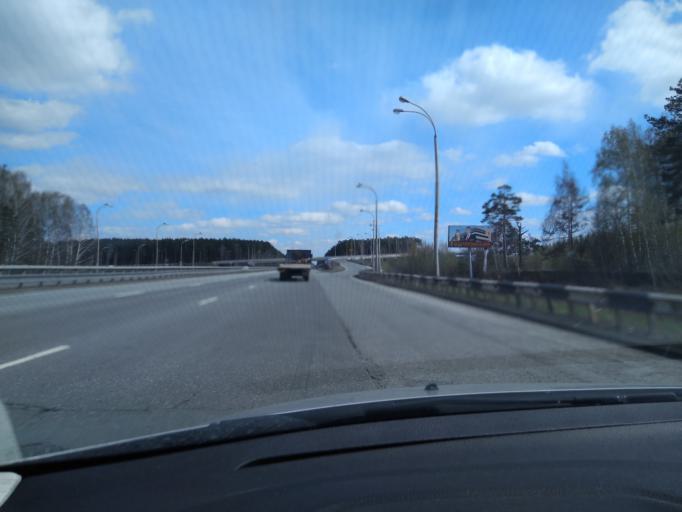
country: RU
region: Sverdlovsk
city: Shuvakish
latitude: 56.8952
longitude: 60.5290
